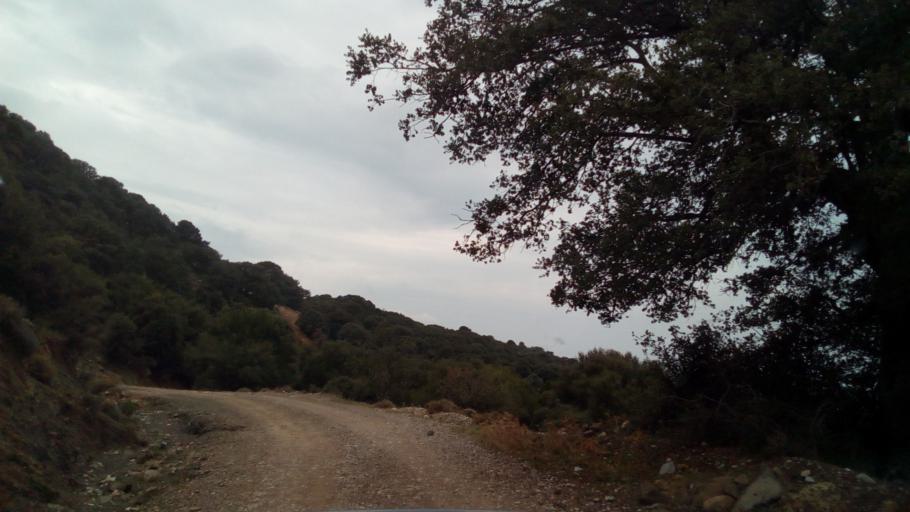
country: GR
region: West Greece
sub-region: Nomos Achaias
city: Selianitika
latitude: 38.4019
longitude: 22.0856
